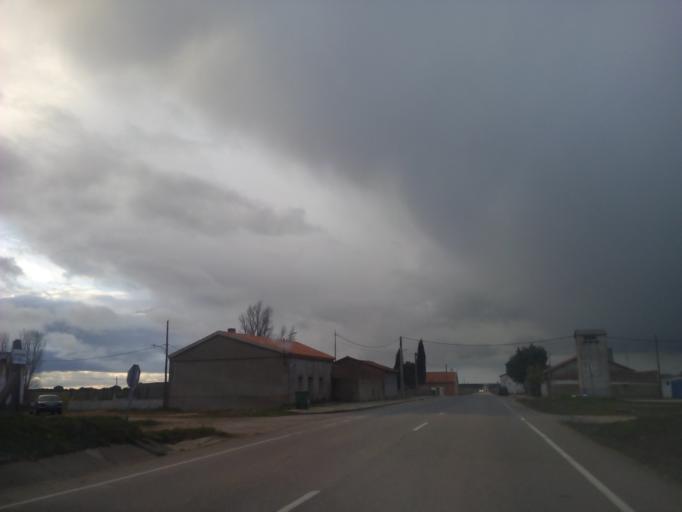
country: ES
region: Castille and Leon
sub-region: Provincia de Salamanca
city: La Fuente de San Esteban
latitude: 40.7757
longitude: -6.2283
